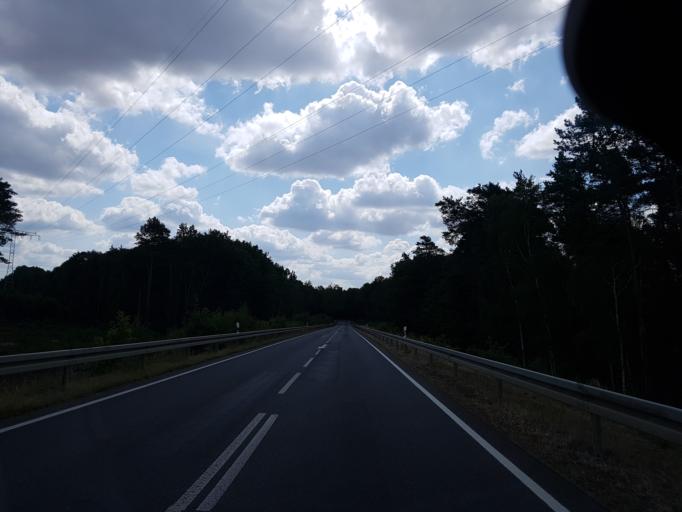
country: DE
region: Brandenburg
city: Drebkau
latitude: 51.6688
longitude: 14.1768
